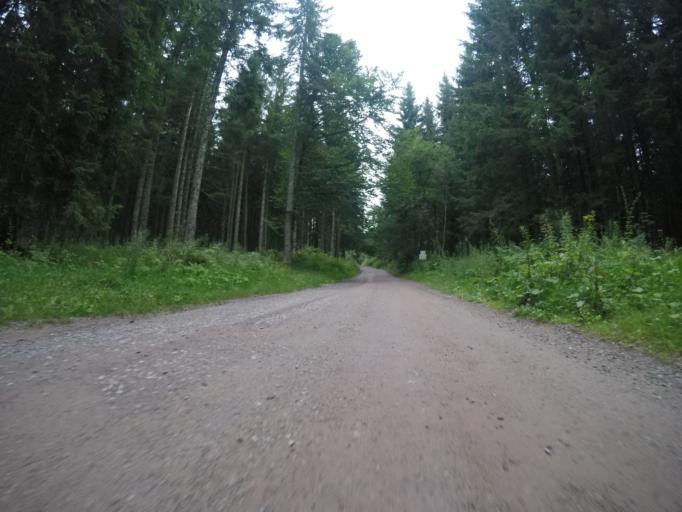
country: DE
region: Baden-Wuerttemberg
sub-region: Freiburg Region
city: Triberg im Schwarzwald
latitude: 48.0953
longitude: 8.2542
